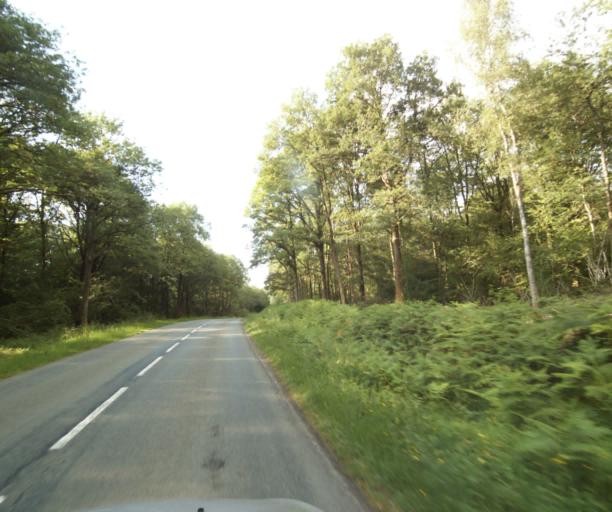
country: FR
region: Champagne-Ardenne
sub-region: Departement des Ardennes
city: Nouzonville
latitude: 49.8239
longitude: 4.6978
